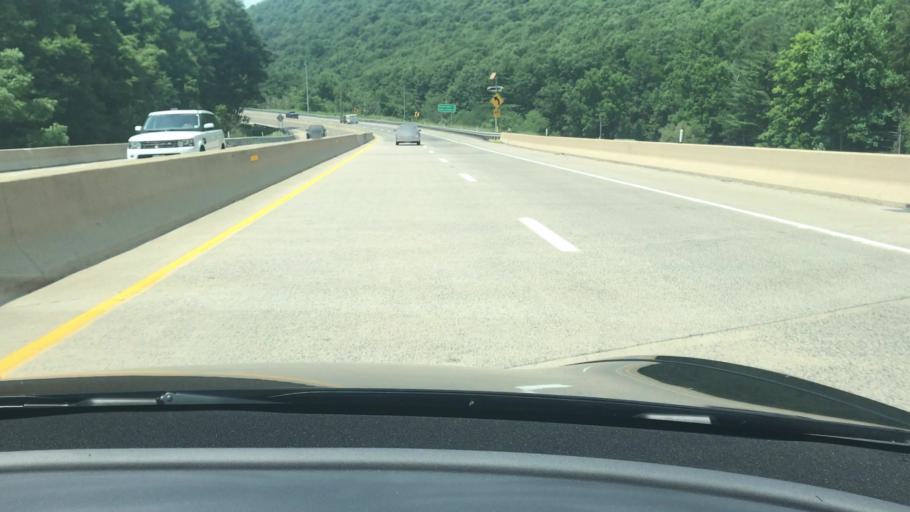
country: US
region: Pennsylvania
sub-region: Mifflin County
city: Milroy
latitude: 40.7313
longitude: -77.6132
